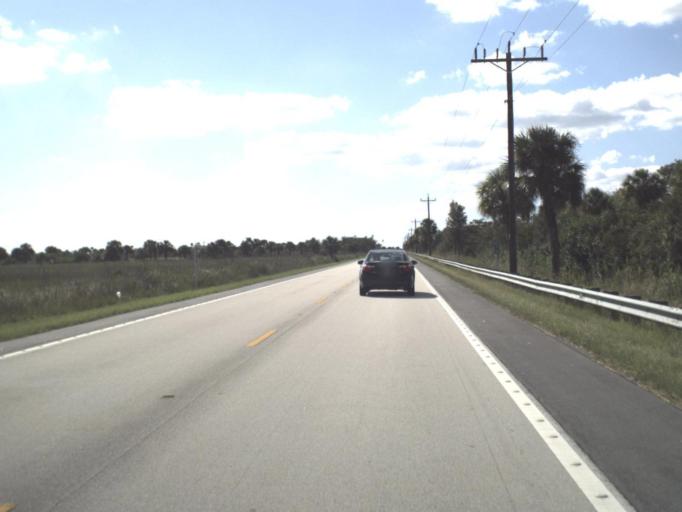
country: US
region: Florida
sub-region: Collier County
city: Marco
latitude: 25.9015
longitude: -81.3157
